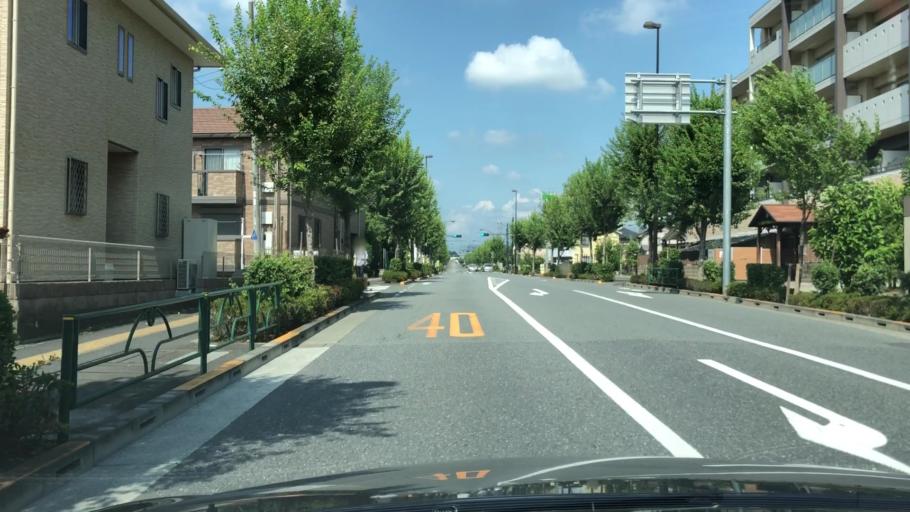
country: JP
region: Tokyo
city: Hino
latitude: 35.6828
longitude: 139.3943
